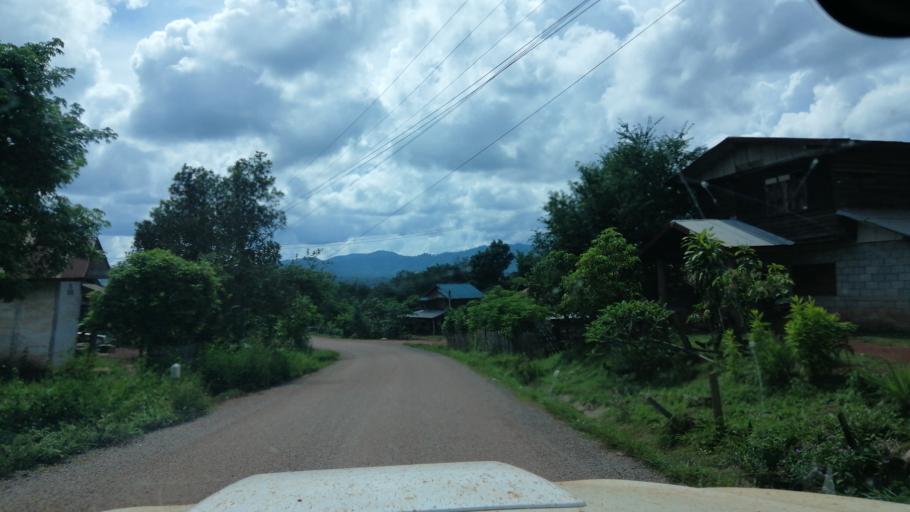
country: TH
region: Uttaradit
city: Ban Khok
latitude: 18.3652
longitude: 101.1420
